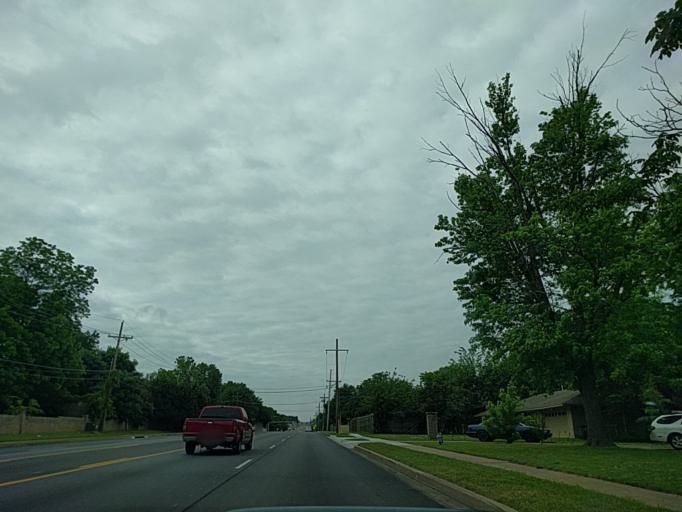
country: US
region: Oklahoma
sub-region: Tulsa County
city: Jenks
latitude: 36.0842
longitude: -95.9045
